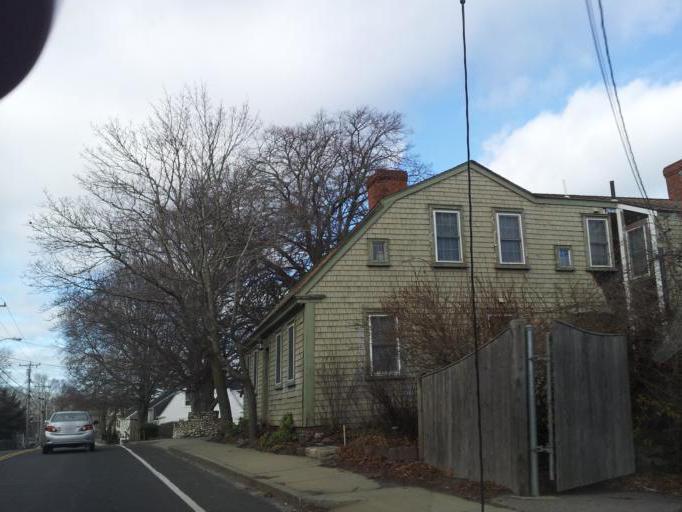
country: US
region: Massachusetts
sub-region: Plymouth County
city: Plymouth
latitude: 41.9483
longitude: -70.6477
